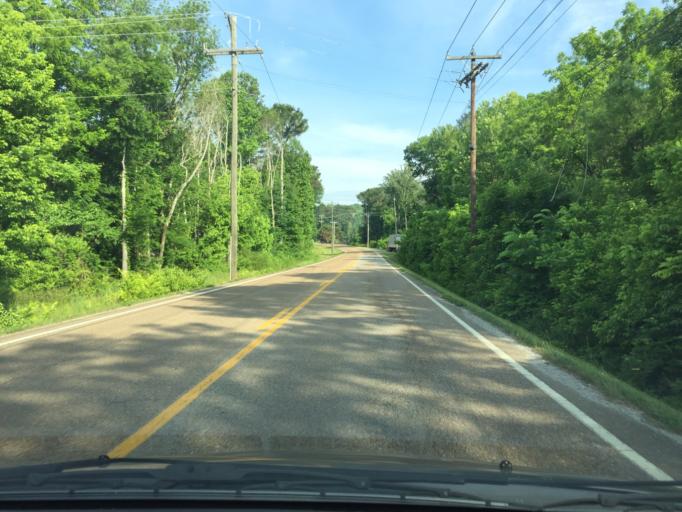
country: US
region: Tennessee
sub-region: Hamilton County
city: Collegedale
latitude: 35.0515
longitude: -85.0424
